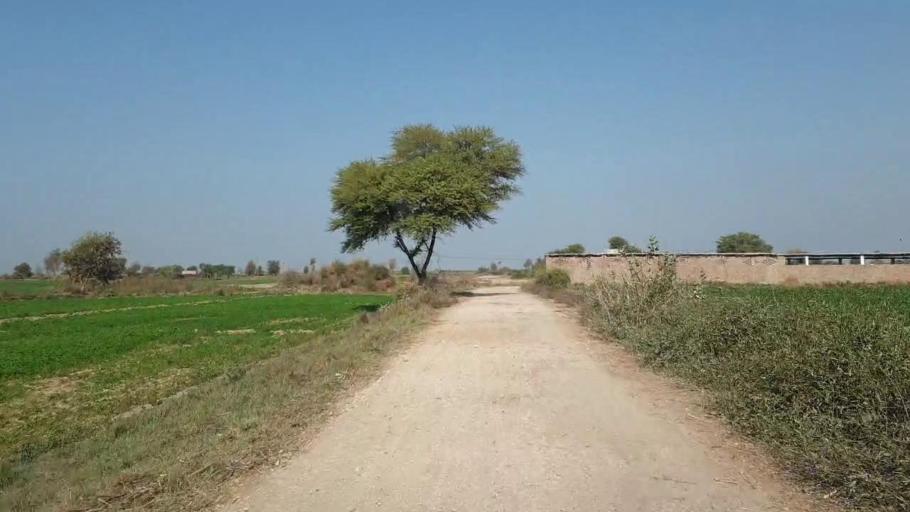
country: PK
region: Sindh
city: Hala
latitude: 25.9525
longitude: 68.4271
